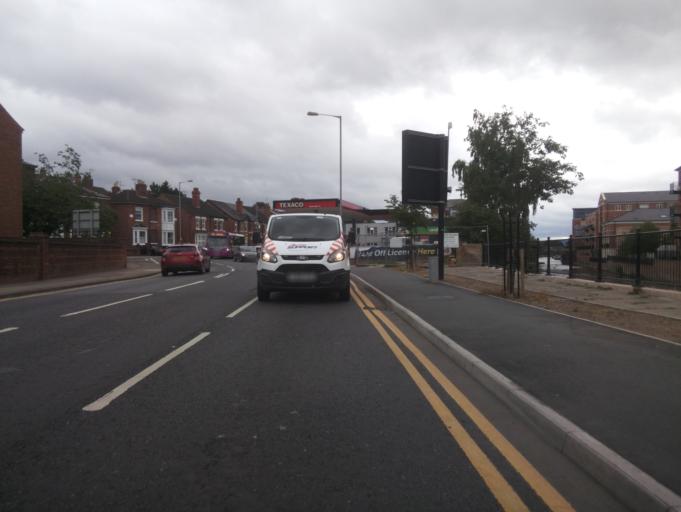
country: GB
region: England
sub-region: Worcestershire
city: Worcester
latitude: 52.1868
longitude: -2.2173
